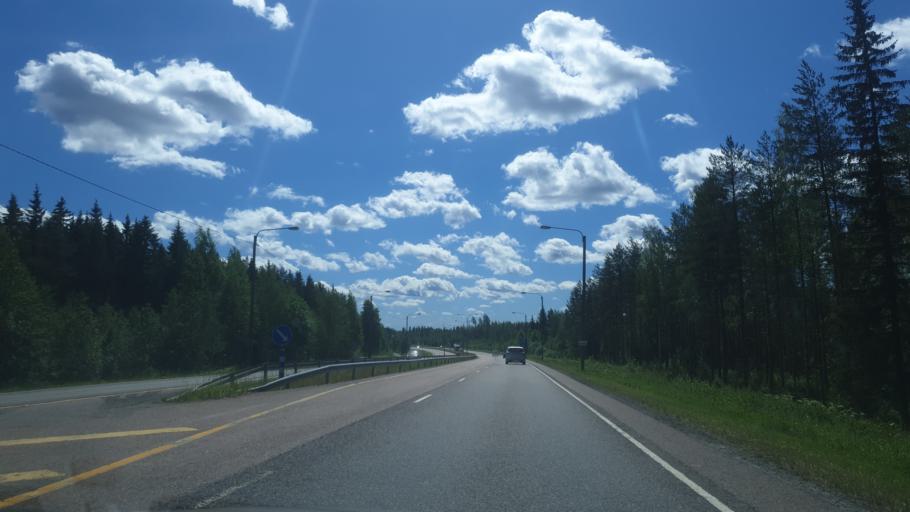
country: FI
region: Northern Savo
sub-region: Varkaus
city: Varkaus
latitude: 62.3414
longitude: 27.8209
